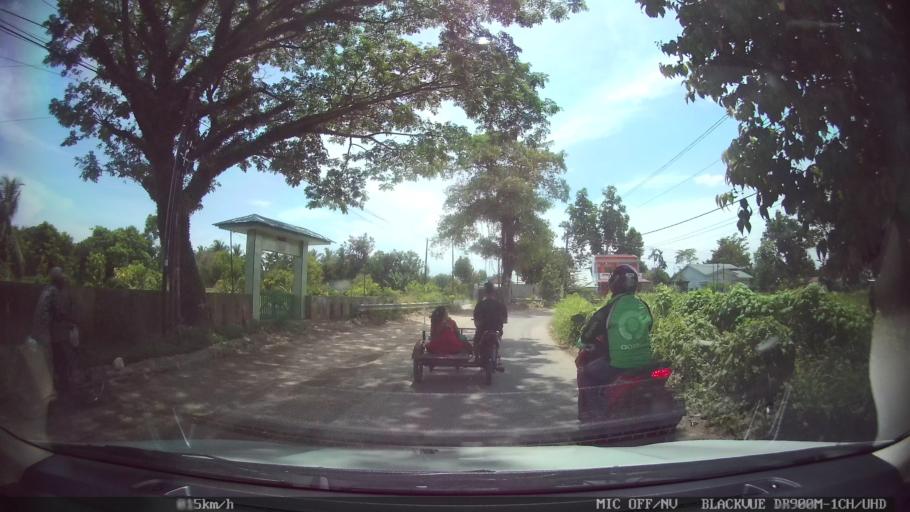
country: ID
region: North Sumatra
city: Binjai
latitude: 3.5940
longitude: 98.4956
